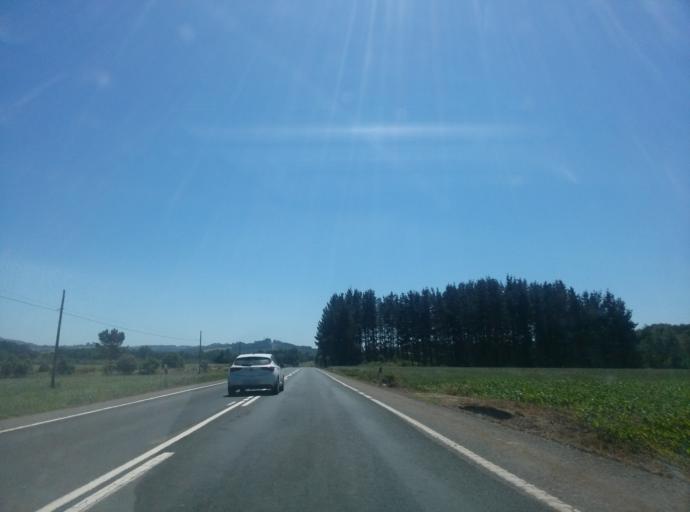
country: ES
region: Galicia
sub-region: Provincia de Lugo
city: Pol
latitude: 43.1782
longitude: -7.3565
